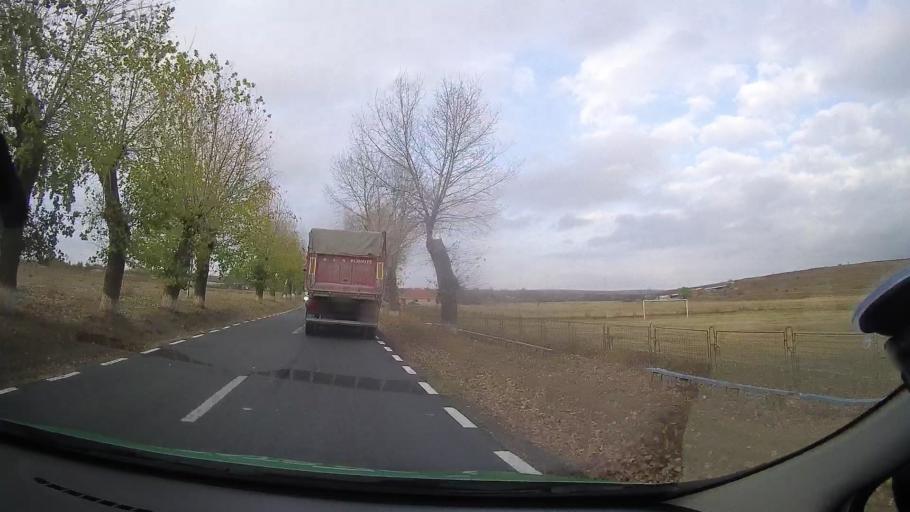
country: RO
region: Constanta
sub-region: Comuna Mircea Voda
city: Mircea Voda
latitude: 44.2726
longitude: 28.1720
